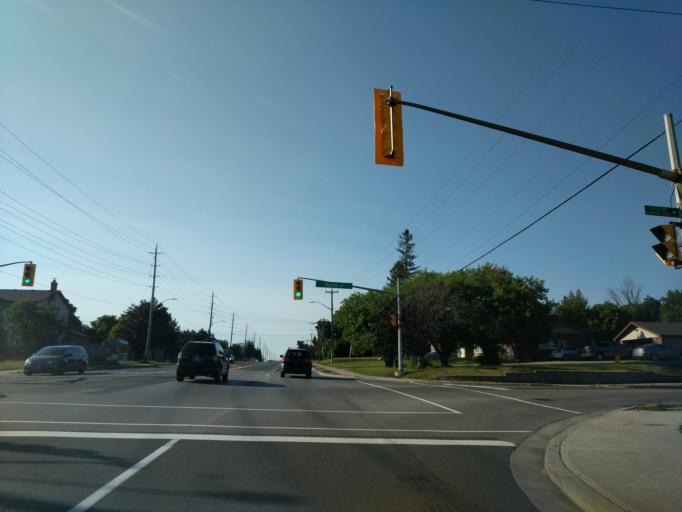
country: CA
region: Ontario
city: Oshawa
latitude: 43.8771
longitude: -78.9086
